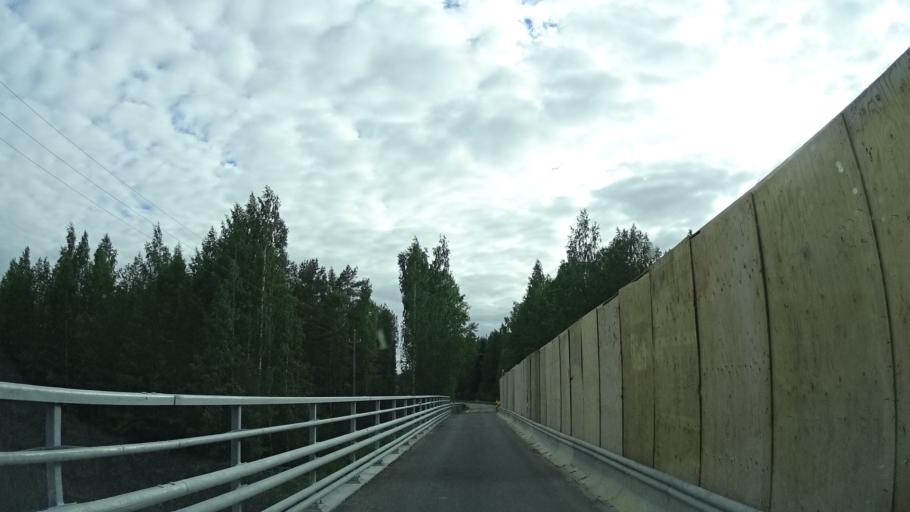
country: FI
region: Central Finland
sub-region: Joutsa
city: Luhanka
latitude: 61.6705
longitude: 25.6225
